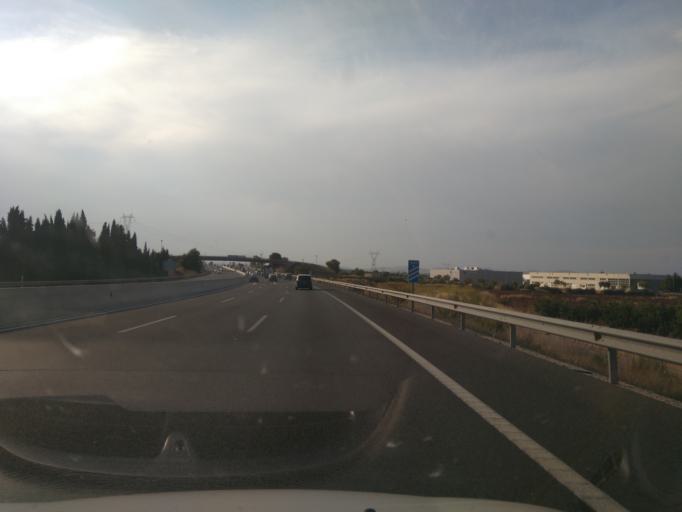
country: ES
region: Valencia
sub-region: Provincia de Valencia
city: Torrent
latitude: 39.4135
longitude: -0.5027
